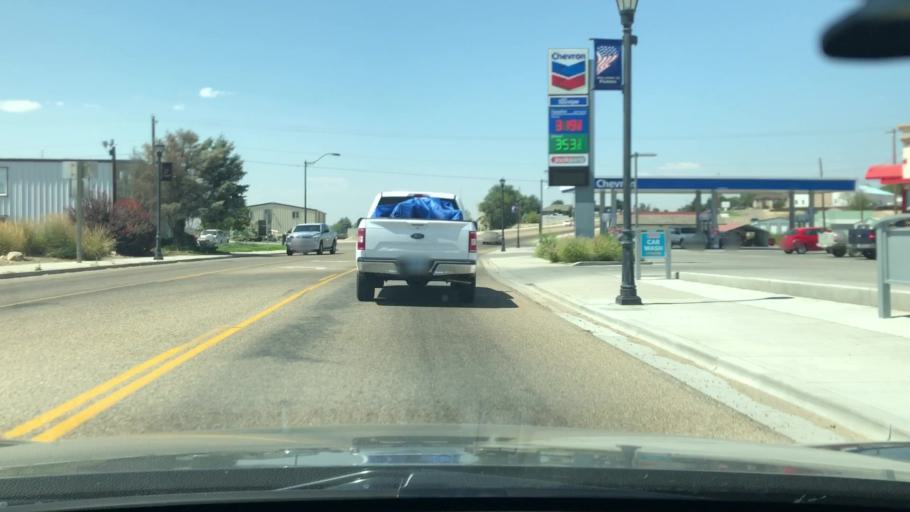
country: US
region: Idaho
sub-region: Canyon County
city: Parma
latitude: 43.7869
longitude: -116.9464
